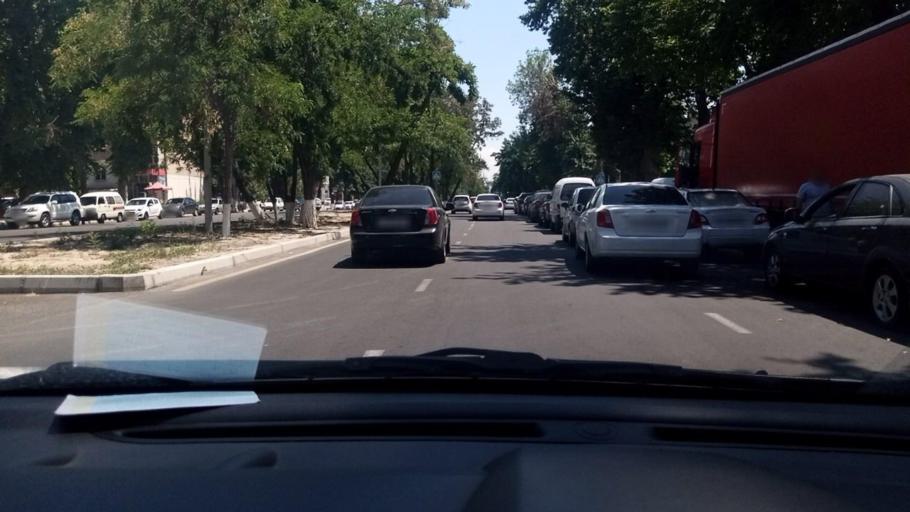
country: UZ
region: Toshkent Shahri
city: Tashkent
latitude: 41.2919
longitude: 69.1993
